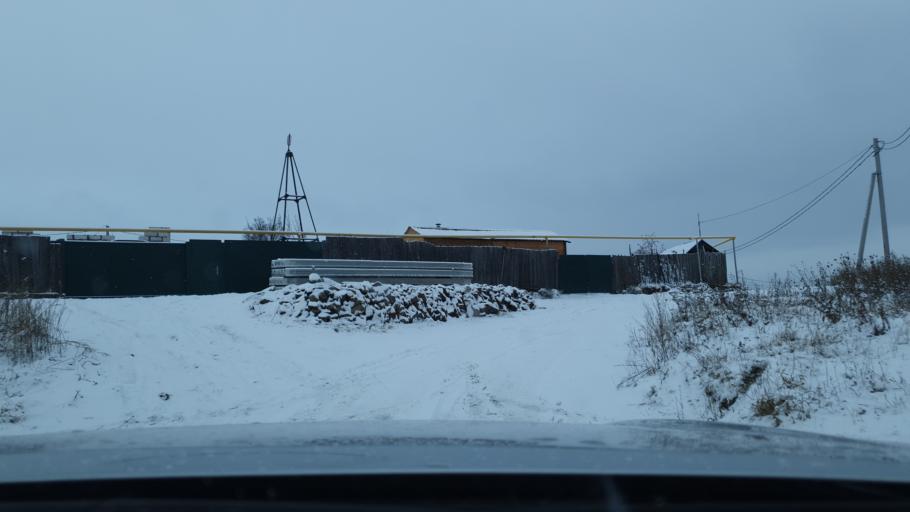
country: RU
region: Sverdlovsk
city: Istok
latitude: 56.7437
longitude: 60.7017
